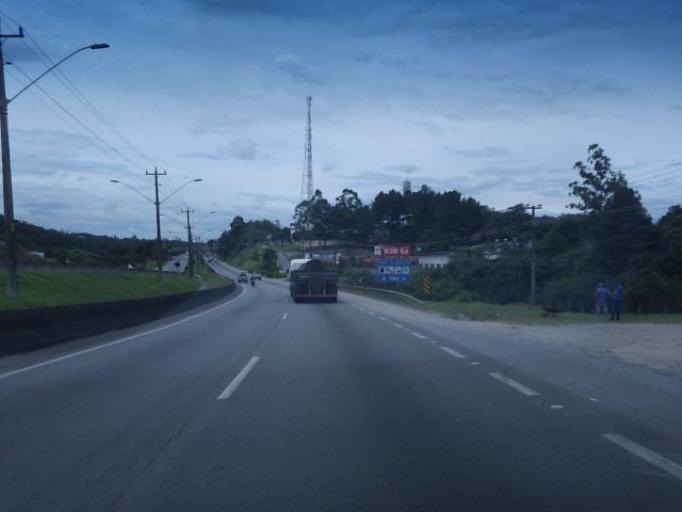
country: BR
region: Sao Paulo
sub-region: Itapecerica Da Serra
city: Itapecerica da Serra
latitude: -23.7429
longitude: -46.8996
